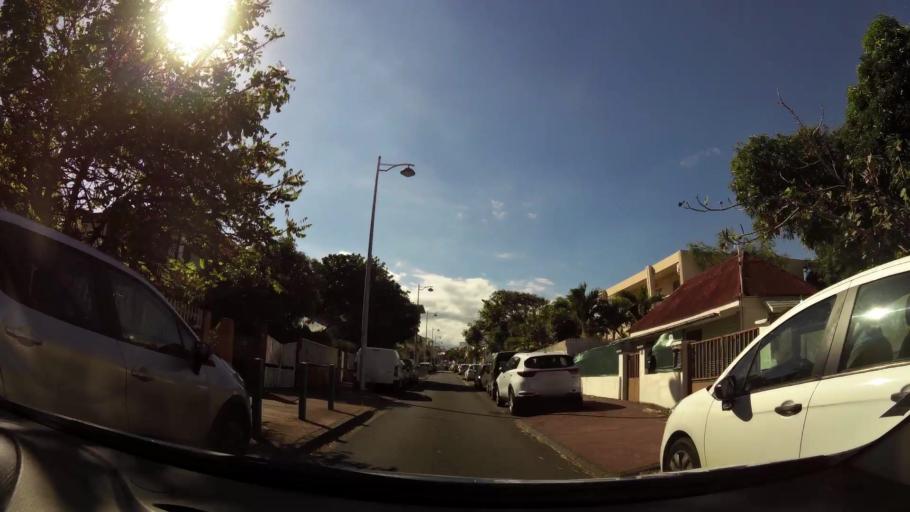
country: RE
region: Reunion
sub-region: Reunion
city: Saint-Pierre
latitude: -21.3397
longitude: 55.4706
